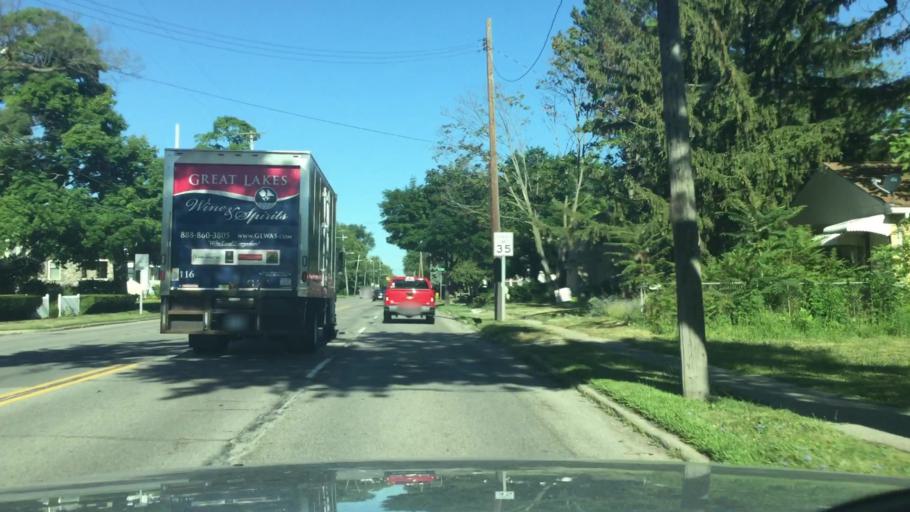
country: US
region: Michigan
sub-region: Saginaw County
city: Saginaw
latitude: 43.4151
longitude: -83.9863
